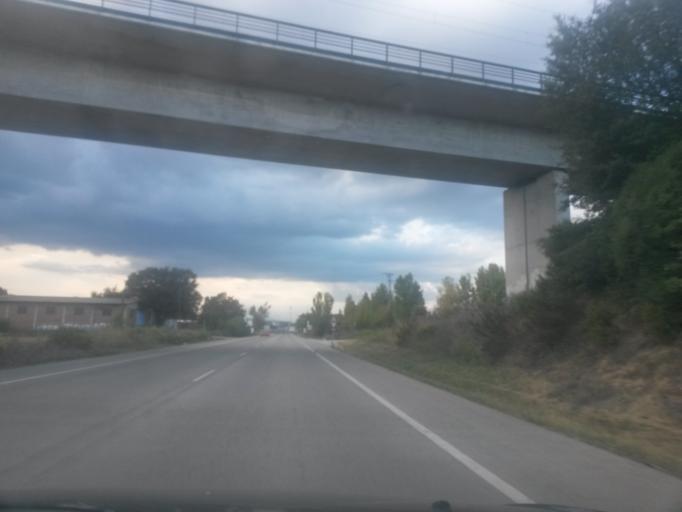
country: ES
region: Catalonia
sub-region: Provincia de Girona
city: Vilobi d'Onyar
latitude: 41.8966
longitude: 2.7731
